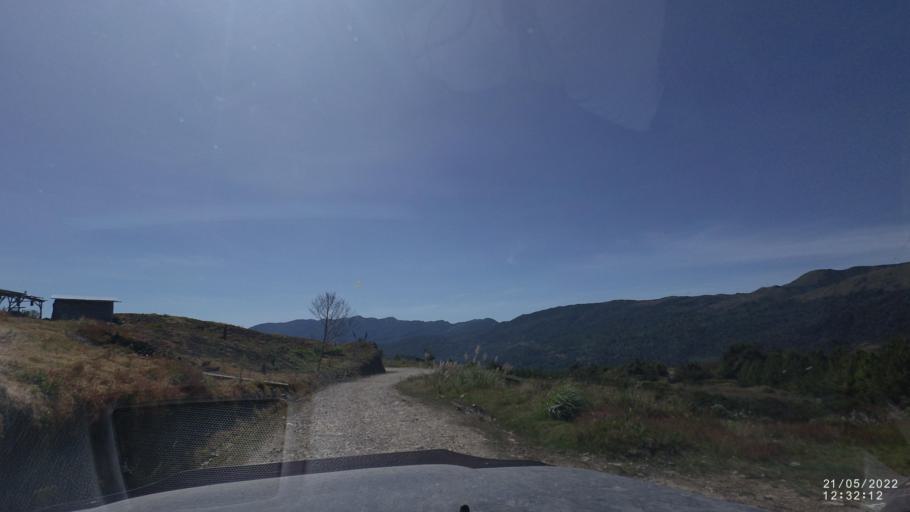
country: BO
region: Cochabamba
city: Colomi
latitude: -17.2073
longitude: -65.9150
